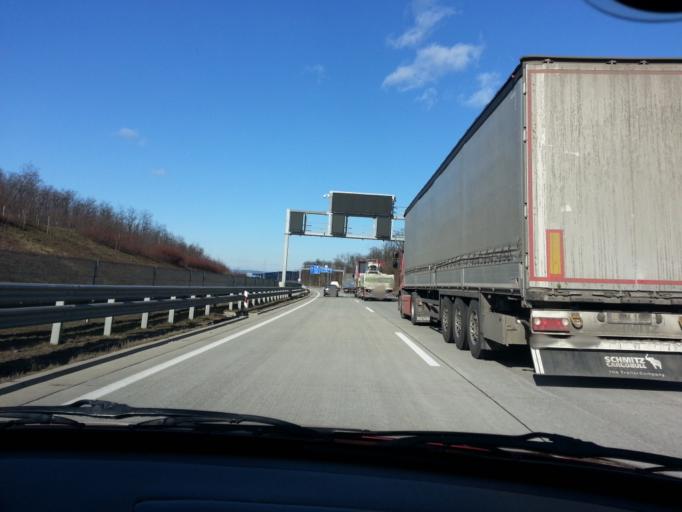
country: HU
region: Pest
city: Szada
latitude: 47.6031
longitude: 19.3210
